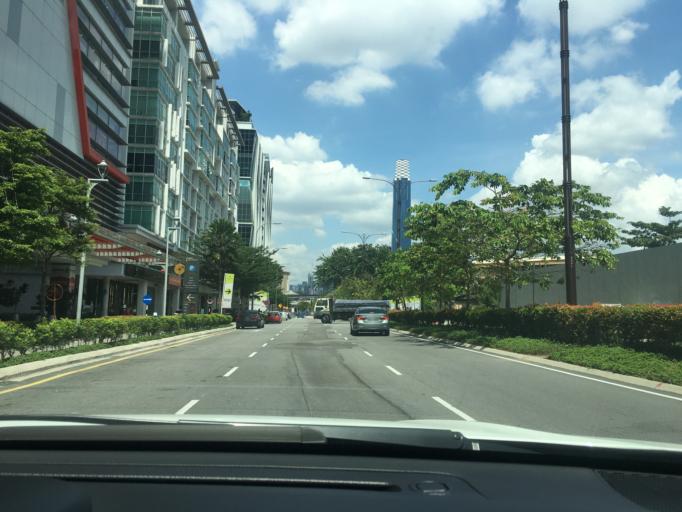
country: MY
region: Kuala Lumpur
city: Kuala Lumpur
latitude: 3.1282
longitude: 101.7247
